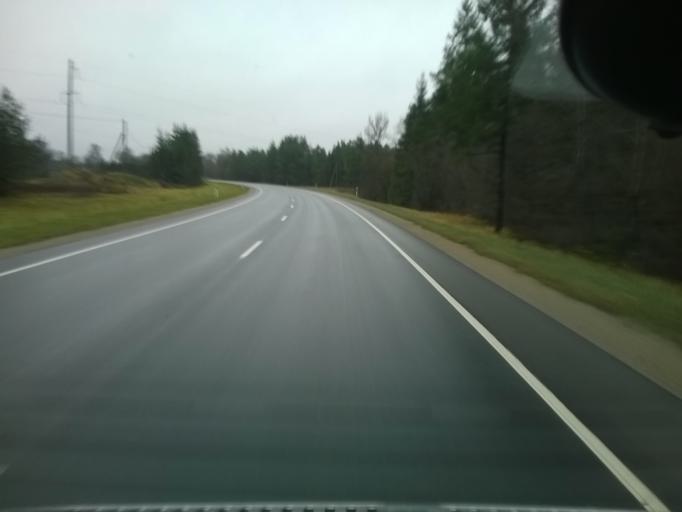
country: EE
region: Harju
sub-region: Nissi vald
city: Turba
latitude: 59.0364
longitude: 24.1660
